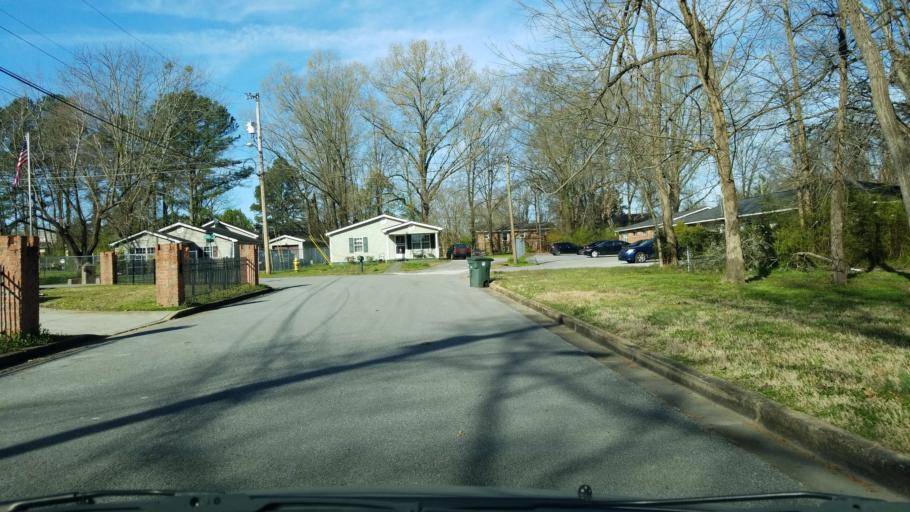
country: US
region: Tennessee
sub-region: Hamilton County
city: East Brainerd
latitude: 35.0408
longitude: -85.1907
